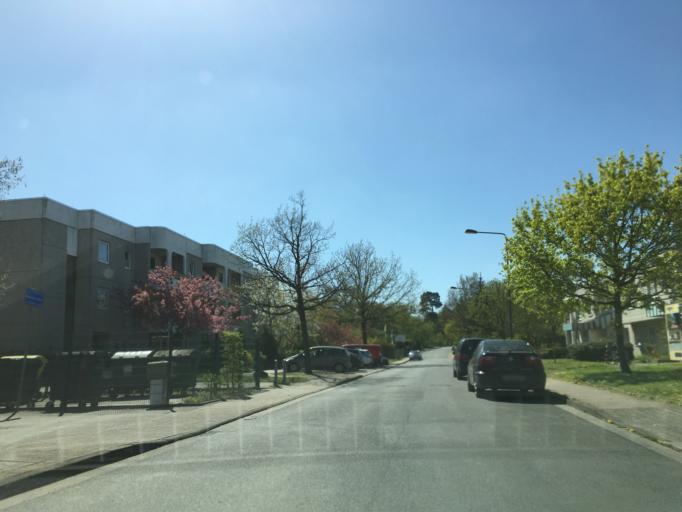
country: DE
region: Hesse
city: Niederrad
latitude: 50.0785
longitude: 8.6024
